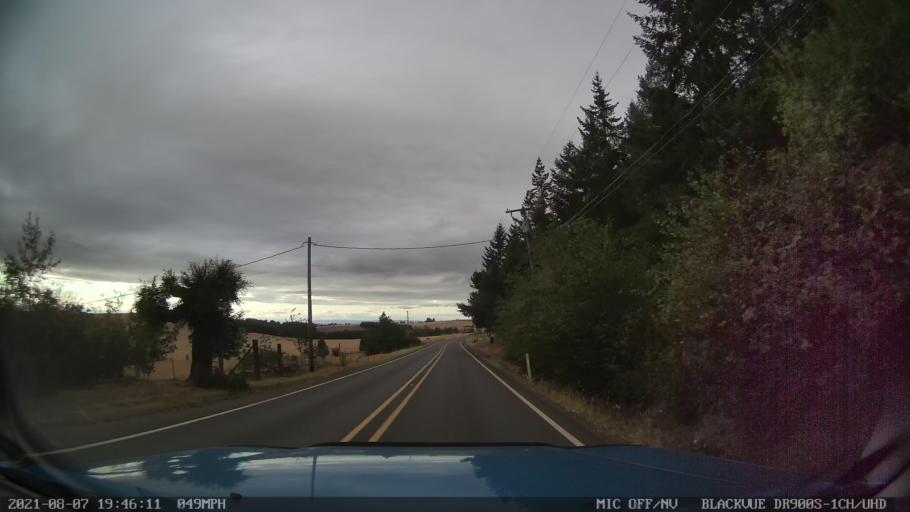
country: US
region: Oregon
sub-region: Marion County
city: Silverton
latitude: 44.9560
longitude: -122.7013
